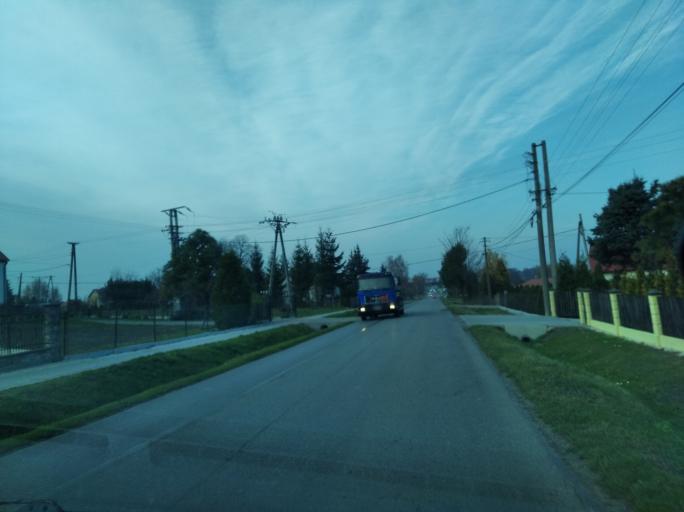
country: PL
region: Subcarpathian Voivodeship
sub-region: Powiat ropczycko-sedziszowski
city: Sedziszow Malopolski
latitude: 50.0607
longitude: 21.7343
